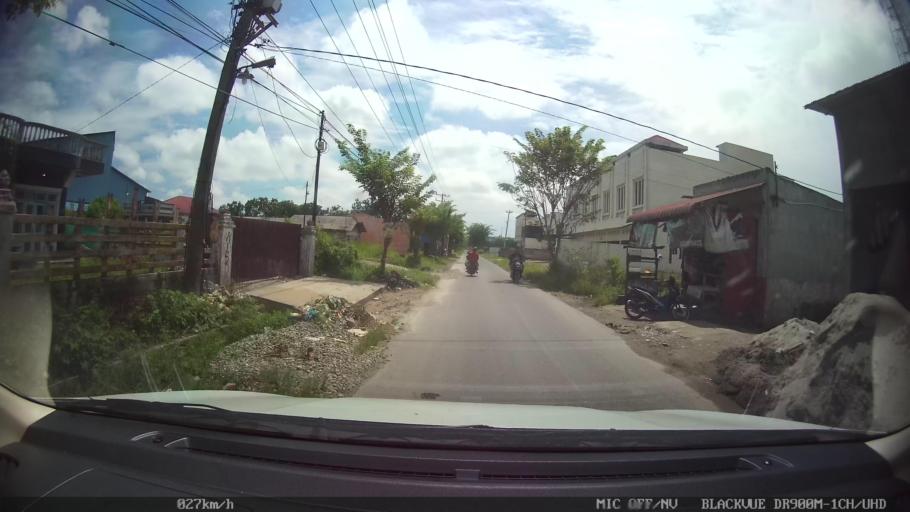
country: ID
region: North Sumatra
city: Percut
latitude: 3.6020
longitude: 98.7732
